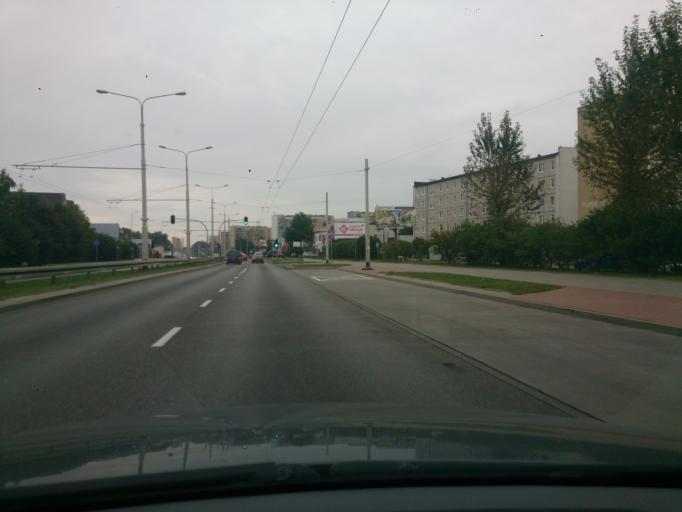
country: PL
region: Pomeranian Voivodeship
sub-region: Gdynia
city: Pogorze
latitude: 54.5479
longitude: 18.4350
